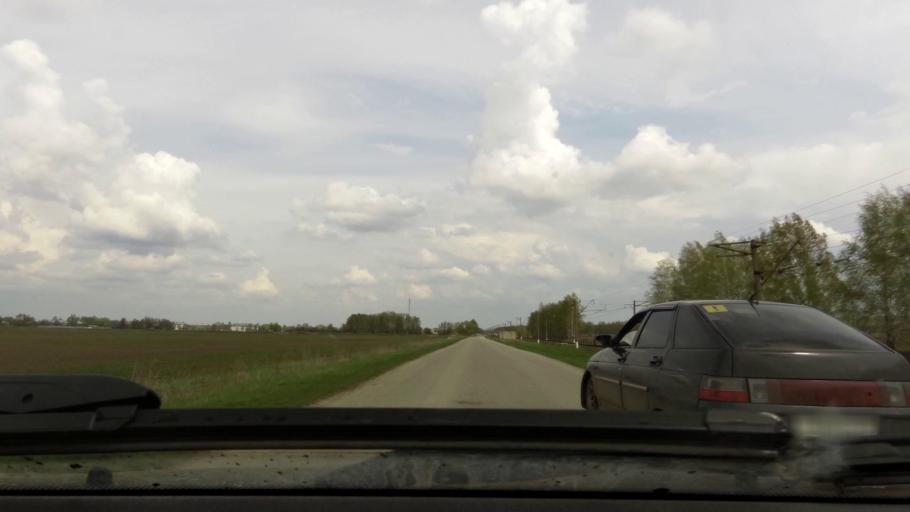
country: RU
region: Rjazan
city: Bagramovo
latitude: 54.7137
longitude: 39.3546
